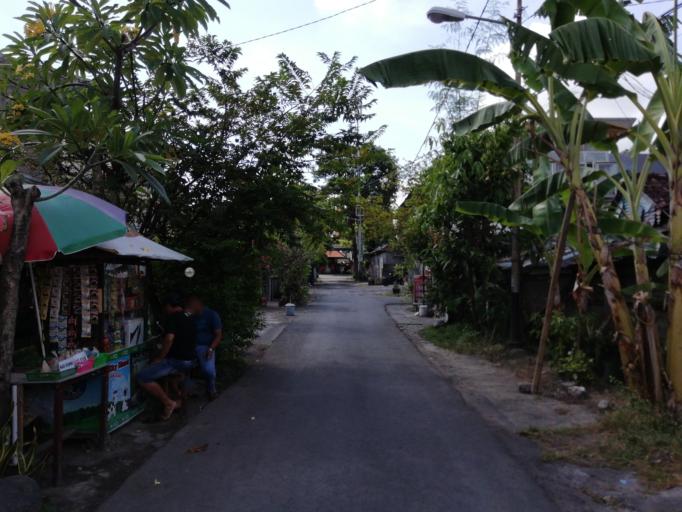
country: ID
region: Bali
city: Denpasar
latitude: -8.6725
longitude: 115.2148
